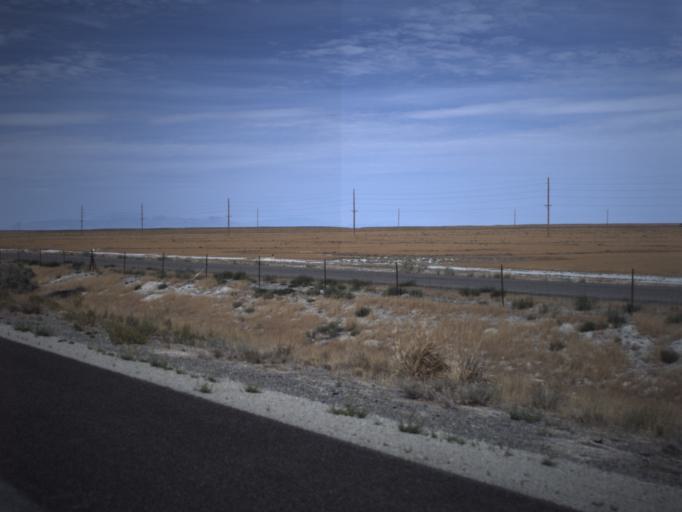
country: US
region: Utah
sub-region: Tooele County
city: Grantsville
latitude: 40.7266
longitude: -113.1957
